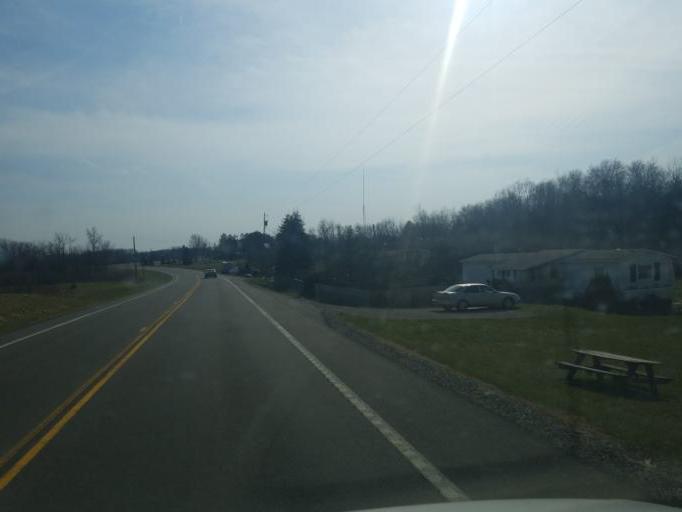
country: US
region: Ohio
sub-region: Logan County
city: Northwood
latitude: 40.4444
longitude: -83.7326
